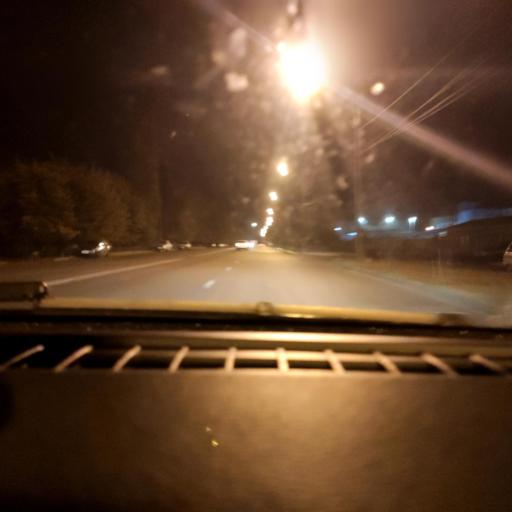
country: RU
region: Voronezj
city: Voronezh
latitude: 51.6518
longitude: 39.2706
